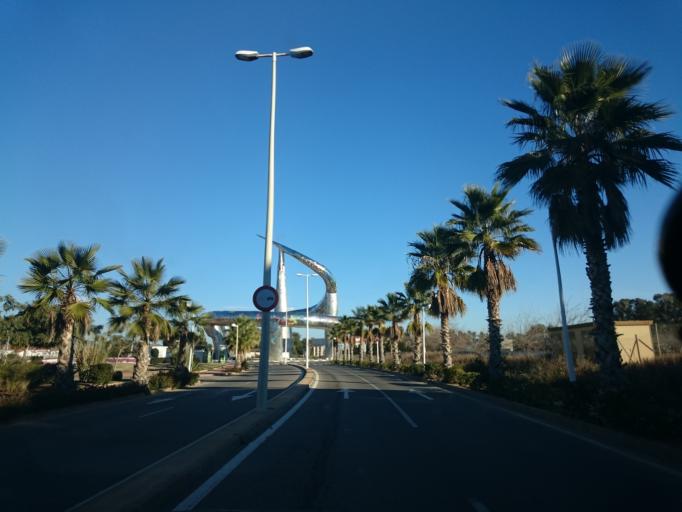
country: ES
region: Valencia
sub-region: Provincia de Castello
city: Orpesa/Oropesa del Mar
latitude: 40.1236
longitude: 0.1572
